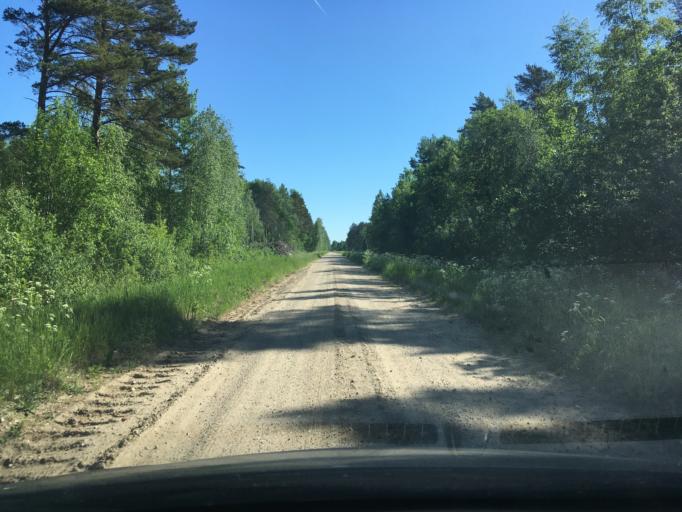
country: EE
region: Laeaene
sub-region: Lihula vald
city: Lihula
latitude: 58.6410
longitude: 23.7675
